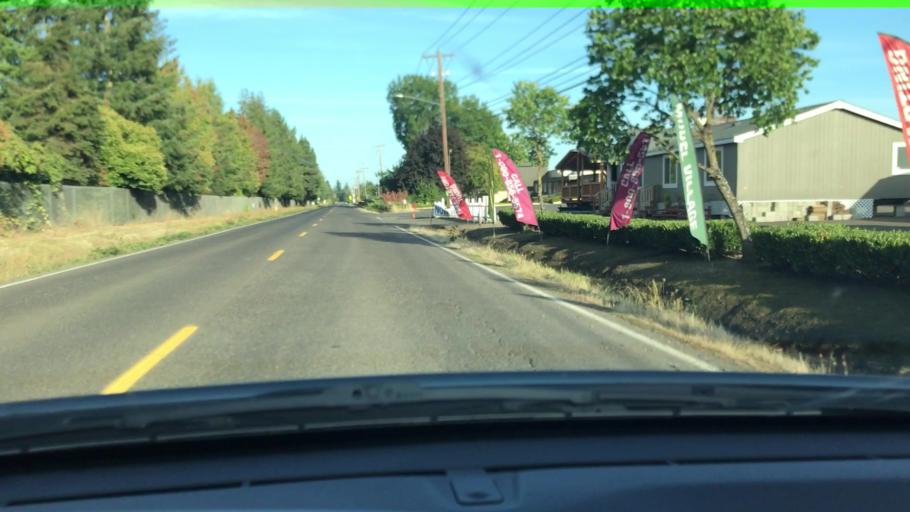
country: US
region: Oregon
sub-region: Yamhill County
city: McMinnville
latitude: 45.1929
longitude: -123.2048
